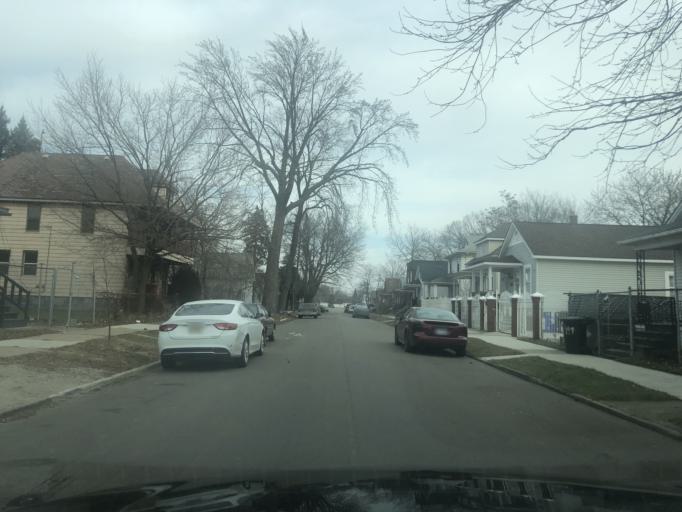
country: US
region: Michigan
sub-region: Wayne County
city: Detroit
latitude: 42.3227
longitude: -83.1024
